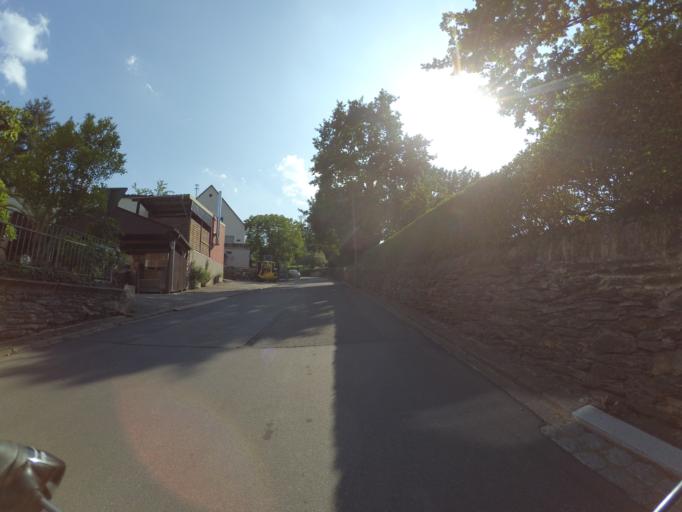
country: DE
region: Rheinland-Pfalz
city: Neumagen-Dhron
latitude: 49.8635
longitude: 6.9040
